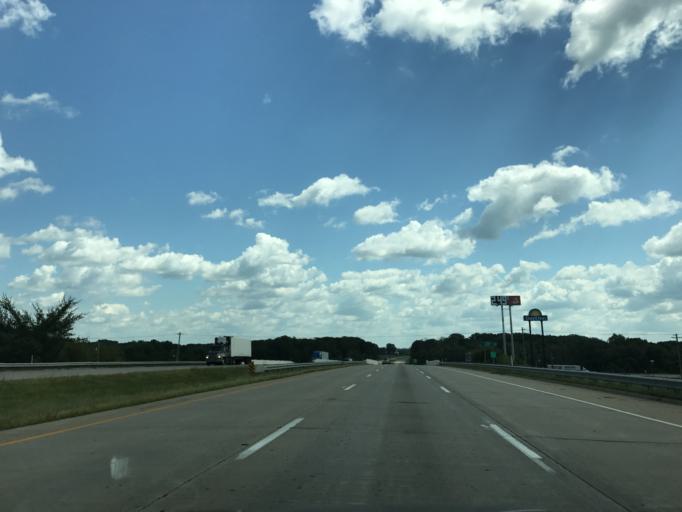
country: US
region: Indiana
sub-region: Marshall County
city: Plymouth
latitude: 41.3619
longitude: -86.3143
